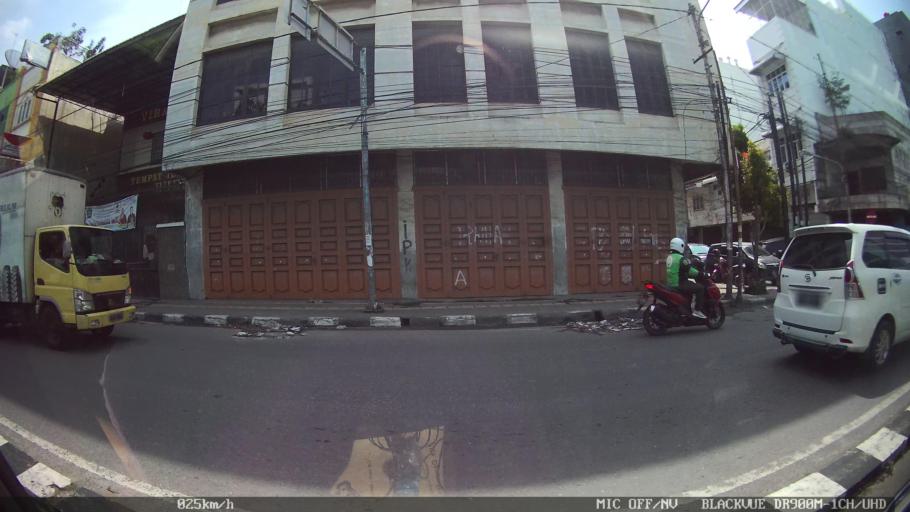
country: ID
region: North Sumatra
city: Medan
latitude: 3.5868
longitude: 98.6830
